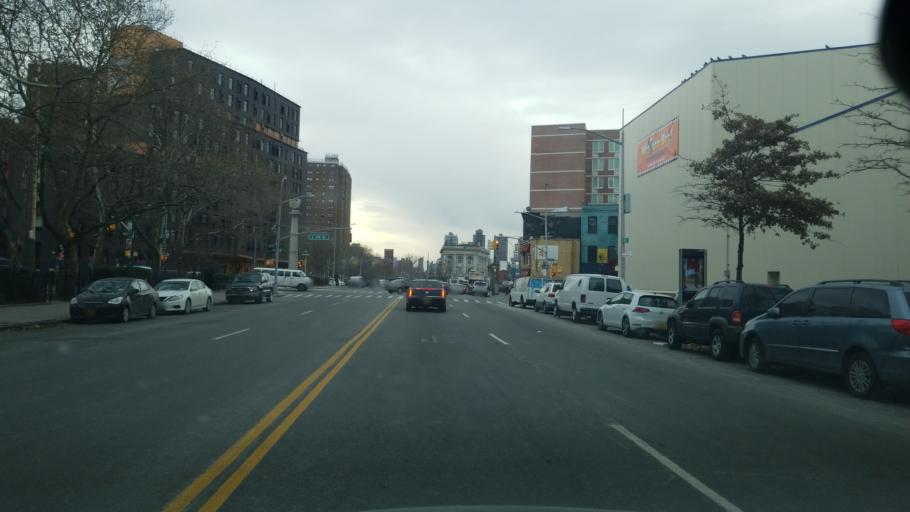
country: US
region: New York
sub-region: New York County
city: Manhattan
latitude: 40.8123
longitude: -73.9263
